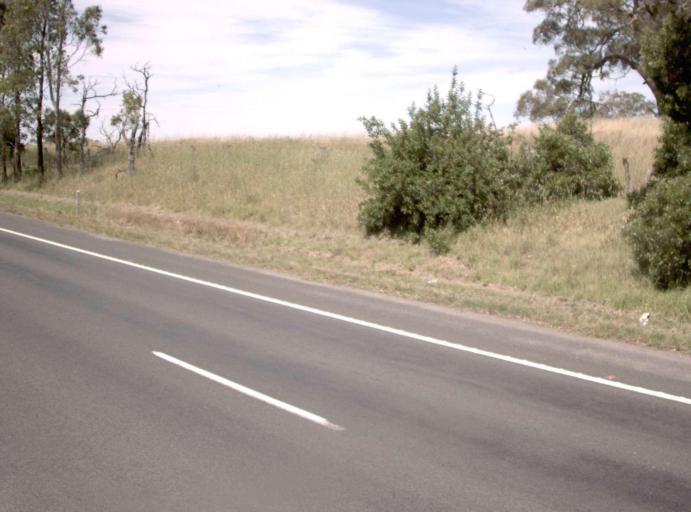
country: AU
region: Victoria
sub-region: Latrobe
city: Traralgon
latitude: -38.1601
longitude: 146.7068
